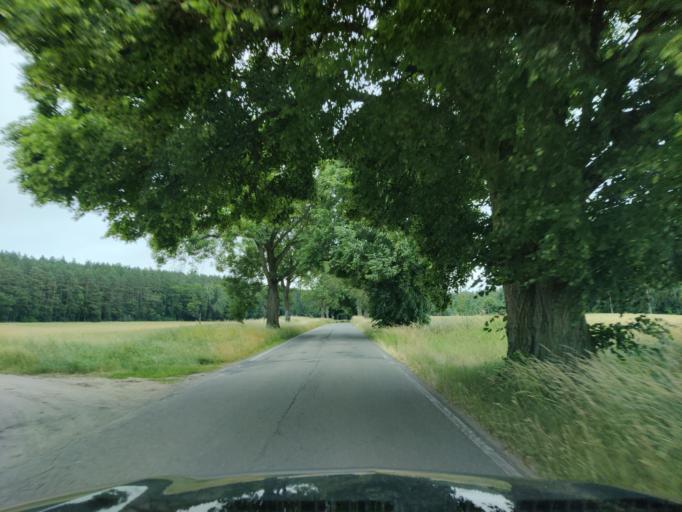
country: PL
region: Warmian-Masurian Voivodeship
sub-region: Powiat gizycki
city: Ryn
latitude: 53.8976
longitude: 21.5722
